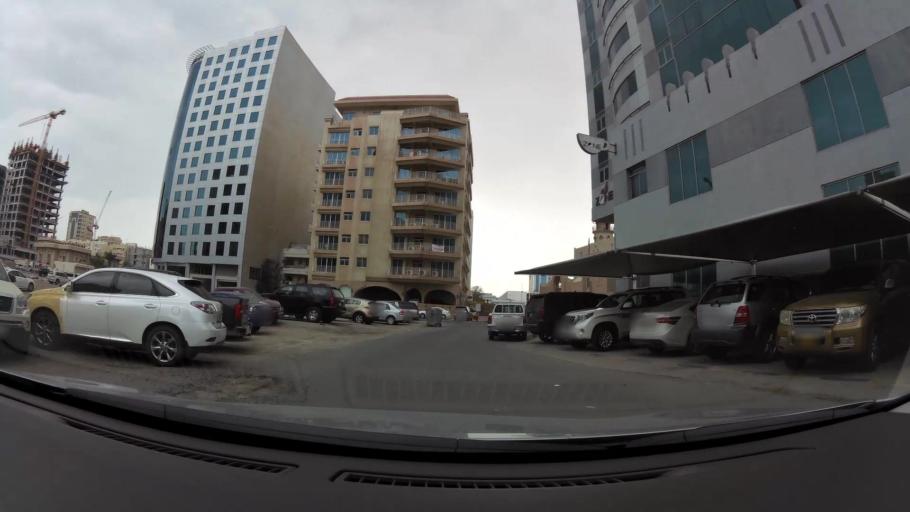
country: QA
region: Baladiyat ad Dawhah
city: Doha
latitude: 25.2880
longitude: 51.5431
